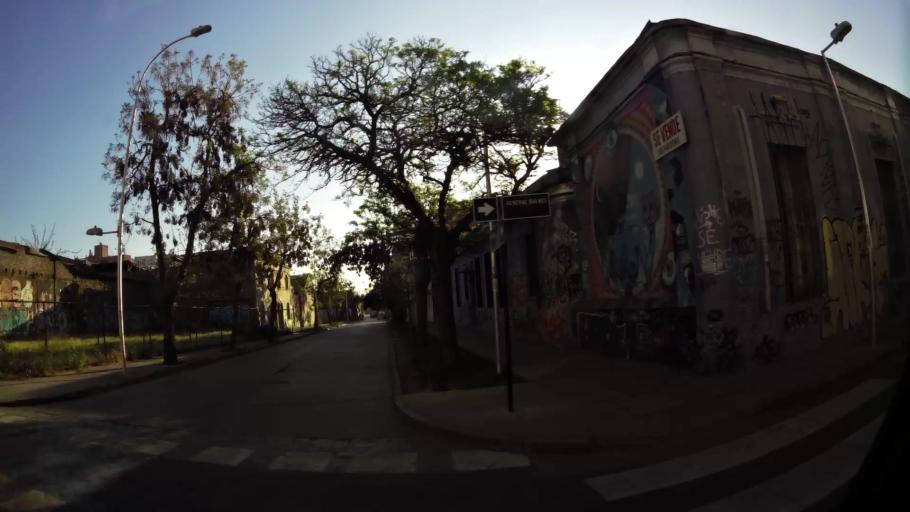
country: CL
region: Santiago Metropolitan
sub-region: Provincia de Santiago
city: Santiago
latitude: -33.4467
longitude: -70.6694
